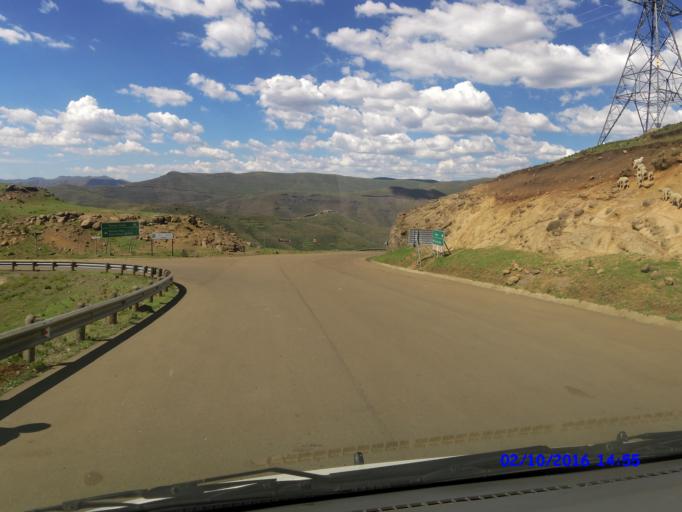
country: LS
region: Maseru
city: Nako
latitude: -29.4741
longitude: 28.0886
